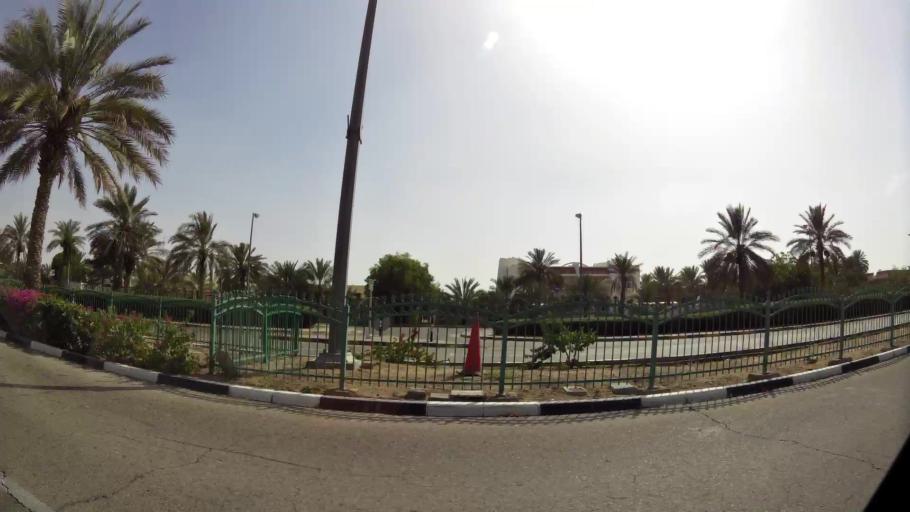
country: AE
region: Abu Dhabi
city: Al Ain
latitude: 24.2343
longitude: 55.6914
